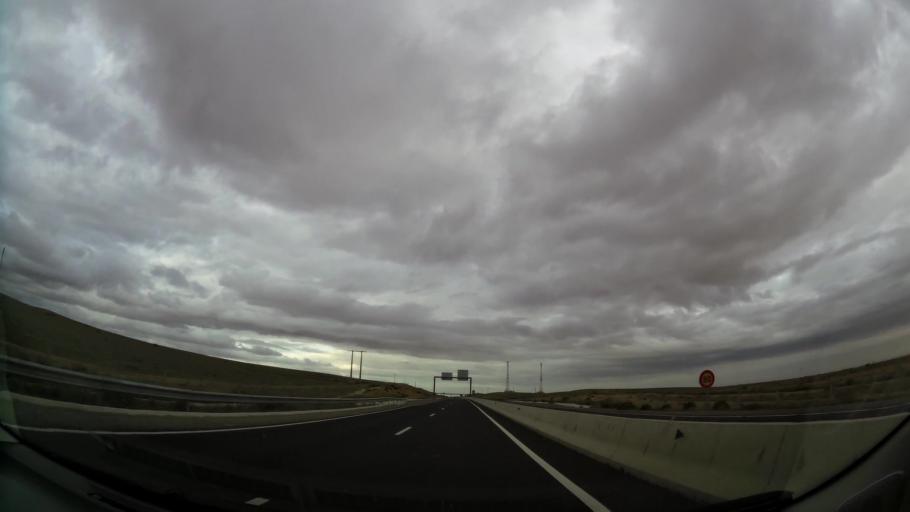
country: MA
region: Taza-Al Hoceima-Taounate
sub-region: Taza
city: Taza
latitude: 34.3078
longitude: -3.7148
